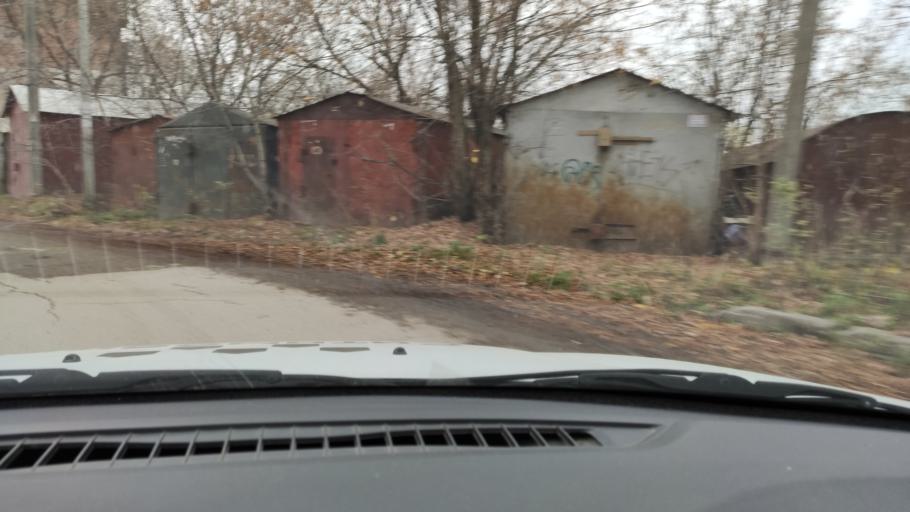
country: RU
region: Perm
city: Perm
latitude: 57.9978
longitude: 56.2354
